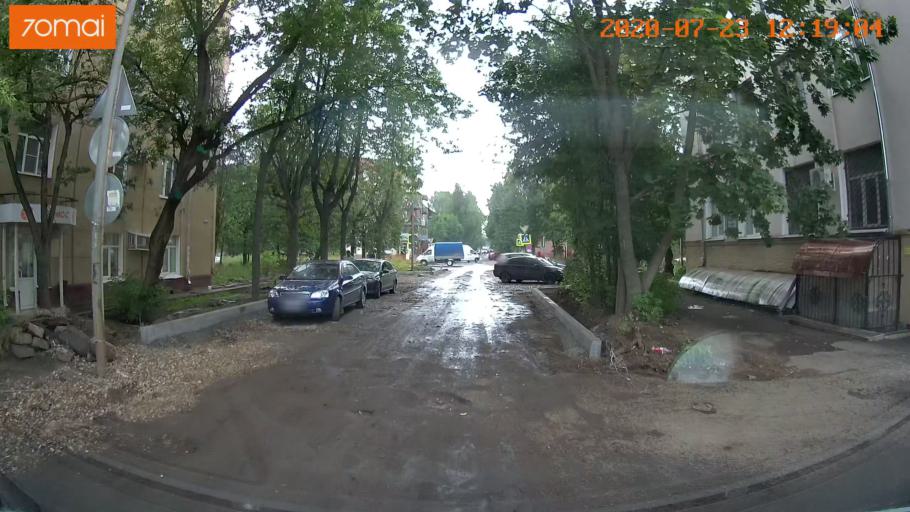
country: RU
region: Ivanovo
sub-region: Gorod Ivanovo
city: Ivanovo
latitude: 57.0075
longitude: 40.9811
